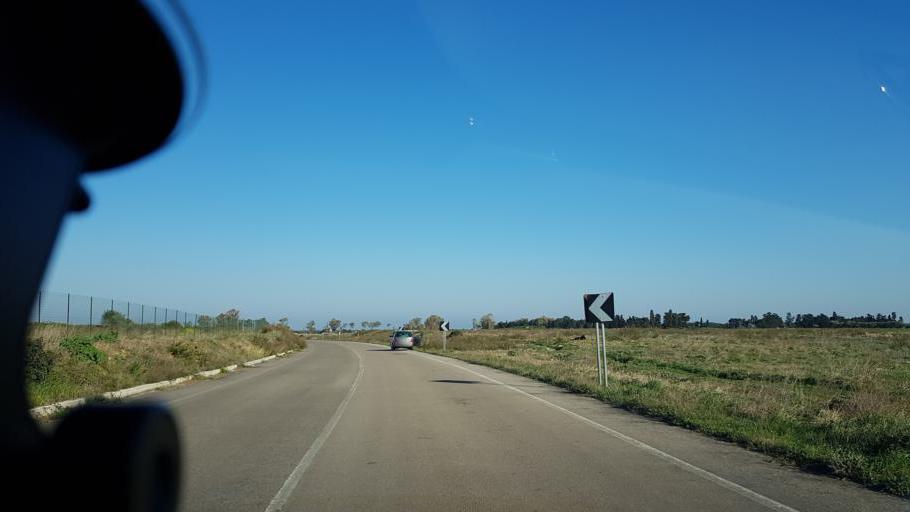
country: IT
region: Apulia
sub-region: Provincia di Lecce
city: Merine
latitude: 40.3940
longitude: 18.2576
